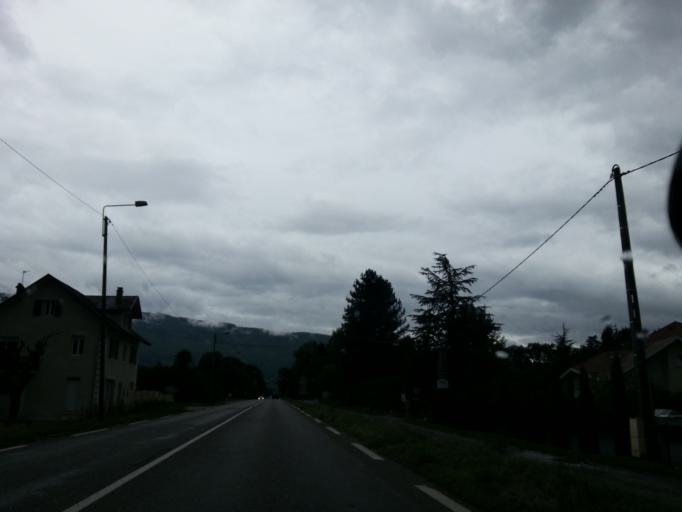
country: FR
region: Rhone-Alpes
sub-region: Departement de la Haute-Savoie
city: Talloires
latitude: 45.8285
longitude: 6.1912
